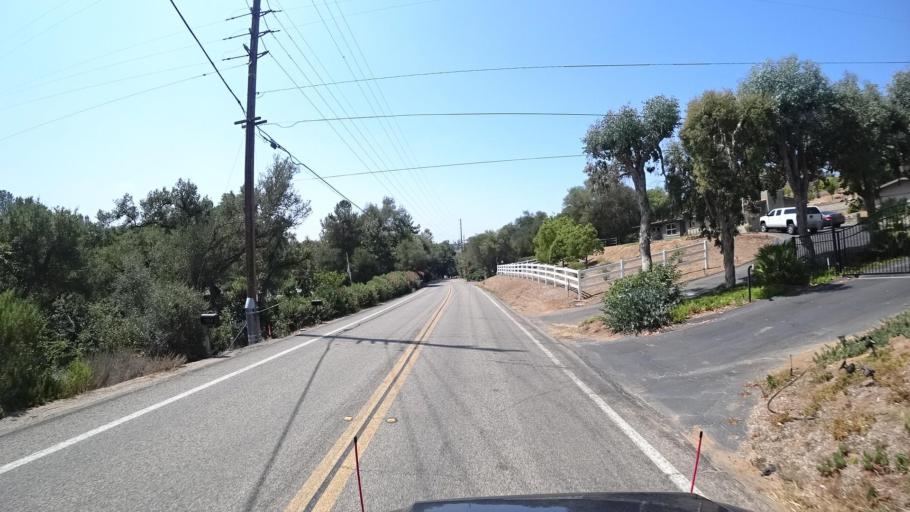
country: US
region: California
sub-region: San Diego County
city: Fallbrook
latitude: 33.3346
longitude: -117.2332
